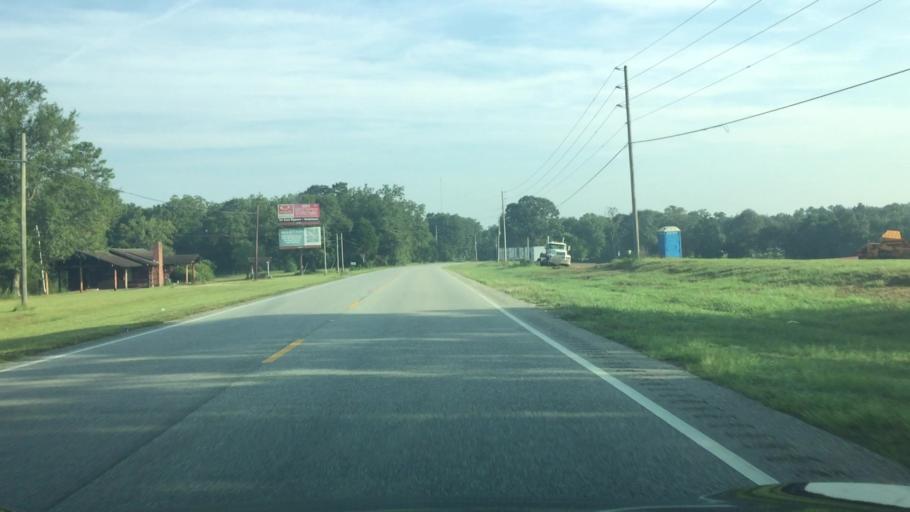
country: US
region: Alabama
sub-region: Covington County
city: Andalusia
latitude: 31.2679
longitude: -86.4734
